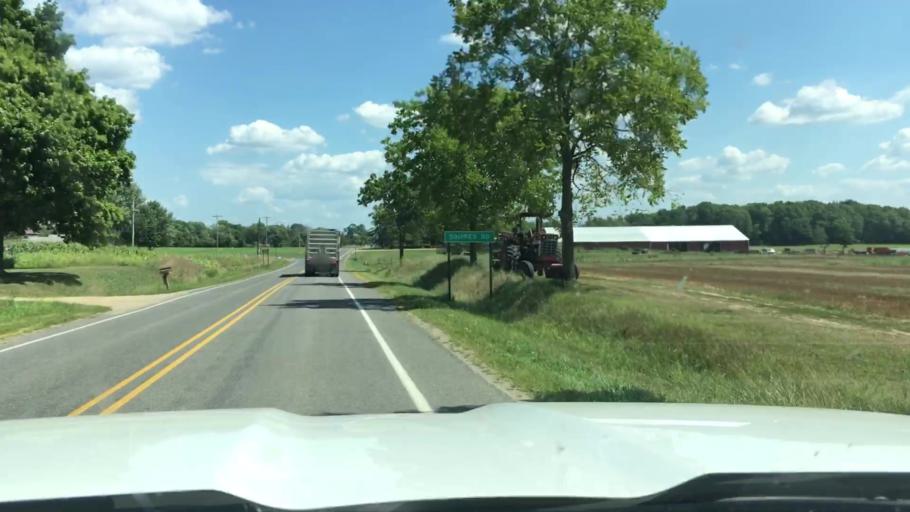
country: US
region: Michigan
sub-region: Muskegon County
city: Ravenna
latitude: 43.2795
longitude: -85.9103
